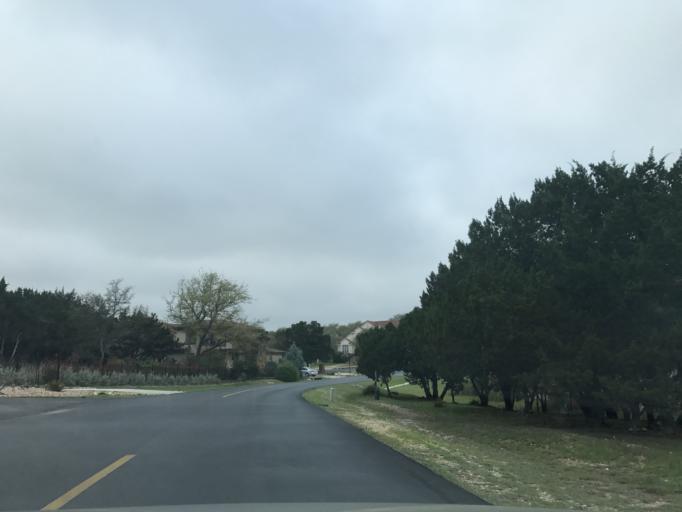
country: US
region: Texas
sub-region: Travis County
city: The Hills
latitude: 30.3421
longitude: -97.9929
